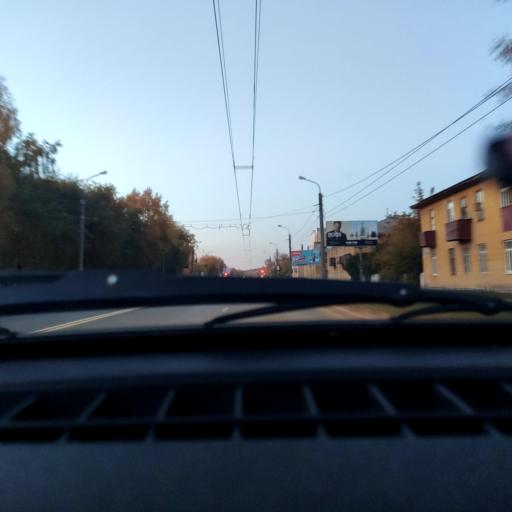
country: RU
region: Bashkortostan
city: Ufa
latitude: 54.7909
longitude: 56.1393
